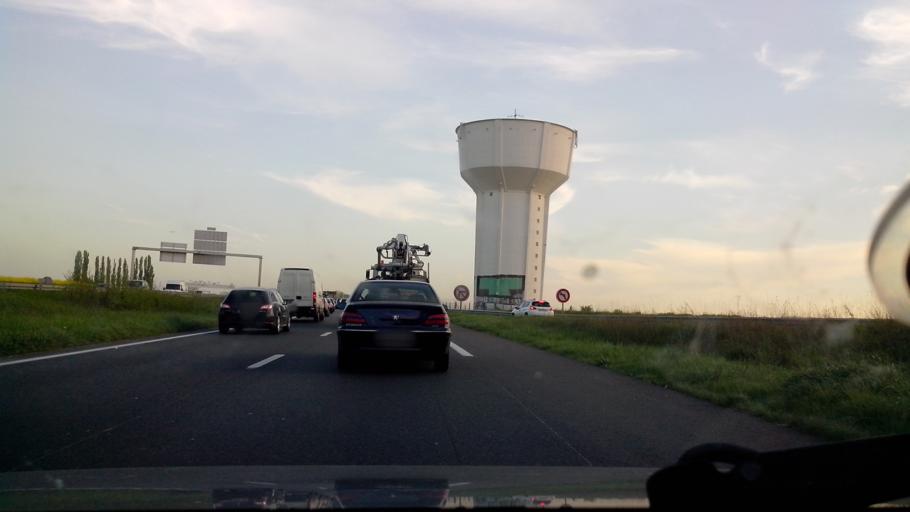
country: FR
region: Ile-de-France
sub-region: Departement de l'Essonne
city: Saclay
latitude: 48.7275
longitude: 2.1655
